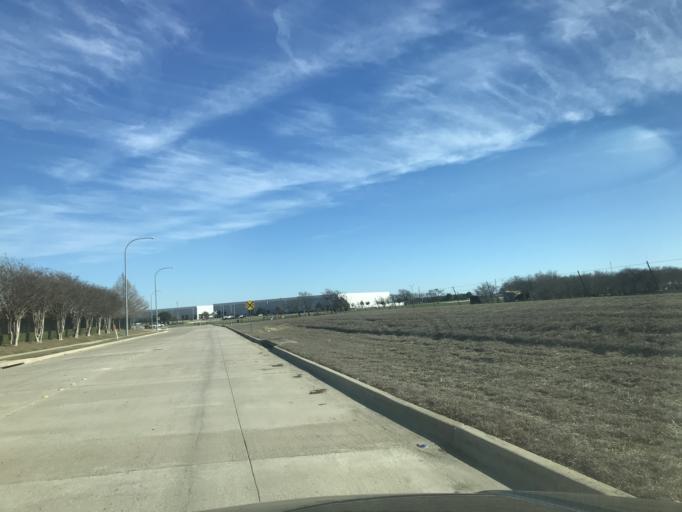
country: US
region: Texas
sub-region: Tarrant County
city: Haltom City
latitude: 32.8157
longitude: -97.3117
